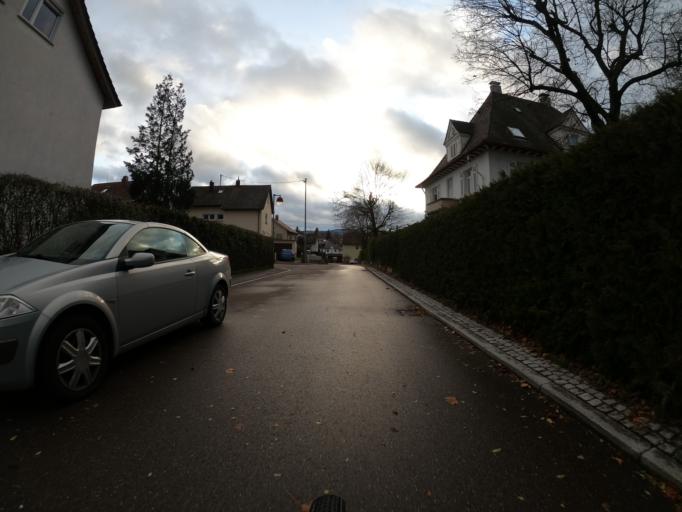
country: DE
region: Baden-Wuerttemberg
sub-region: Regierungsbezirk Stuttgart
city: Salach
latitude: 48.6905
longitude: 9.7445
